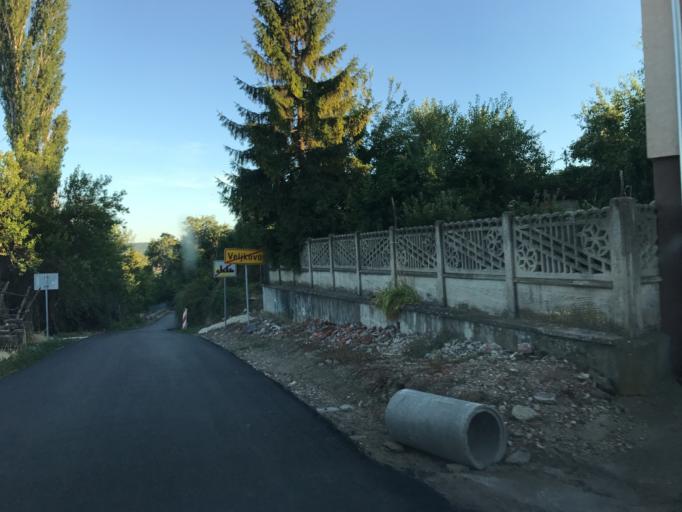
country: BG
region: Vidin
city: Bregovo
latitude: 44.1233
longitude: 22.5988
